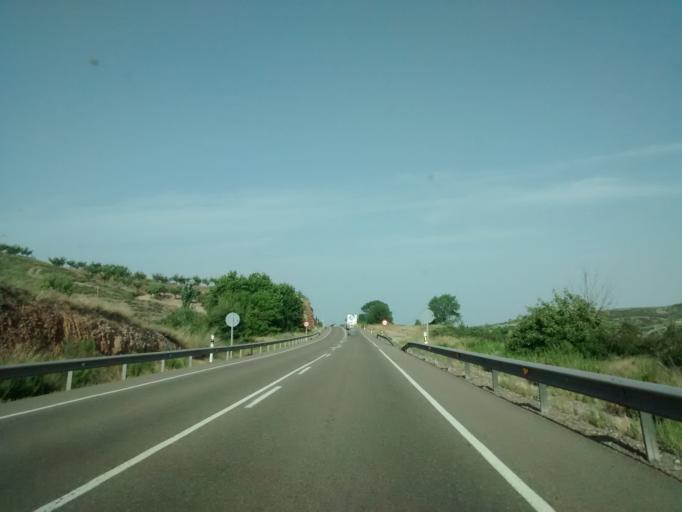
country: ES
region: Aragon
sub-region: Provincia de Zaragoza
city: Bulbuente
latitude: 41.8183
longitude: -1.6163
